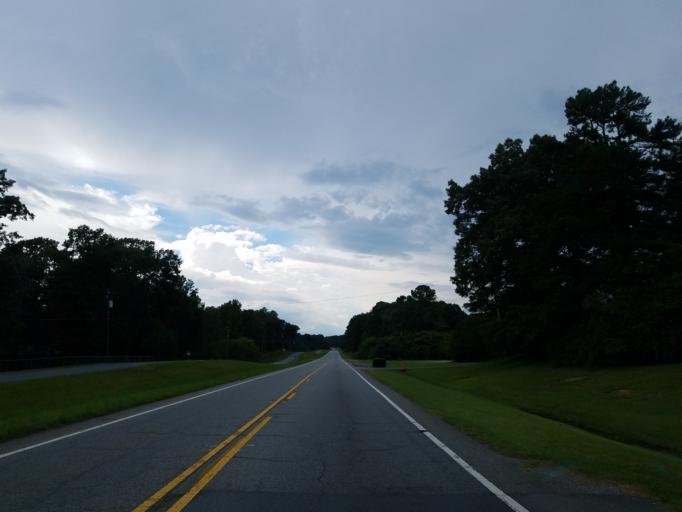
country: US
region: Georgia
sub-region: Bartow County
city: Adairsville
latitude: 34.3011
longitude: -84.8818
